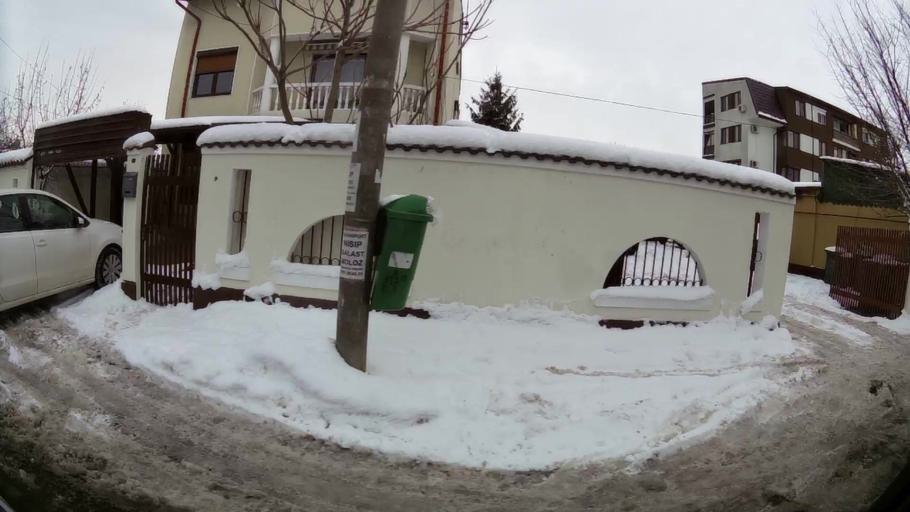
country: RO
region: Bucuresti
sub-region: Municipiul Bucuresti
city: Bucuresti
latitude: 44.3908
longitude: 26.1021
